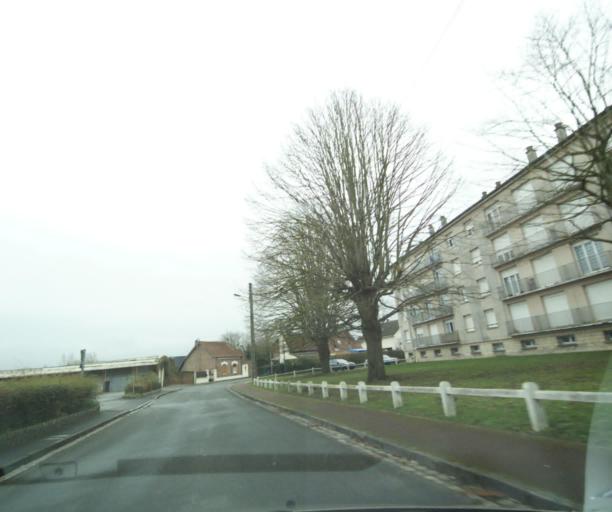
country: FR
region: Picardie
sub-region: Departement de l'Oise
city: Noyon
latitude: 49.5763
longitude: 2.9971
